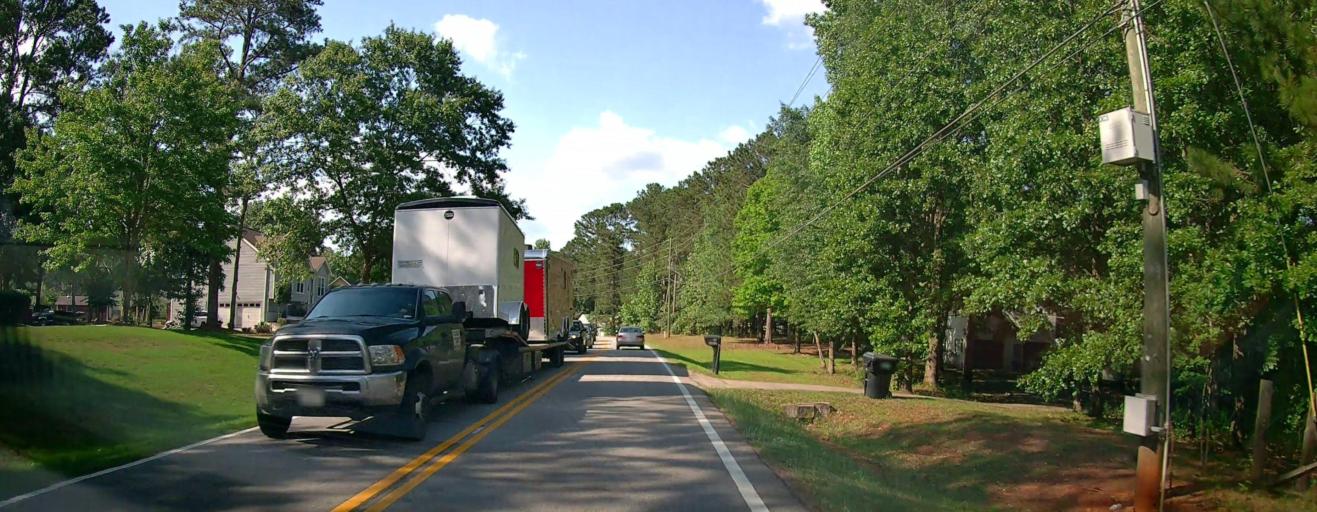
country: US
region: Georgia
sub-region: Henry County
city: Stockbridge
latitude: 33.4719
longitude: -84.2287
